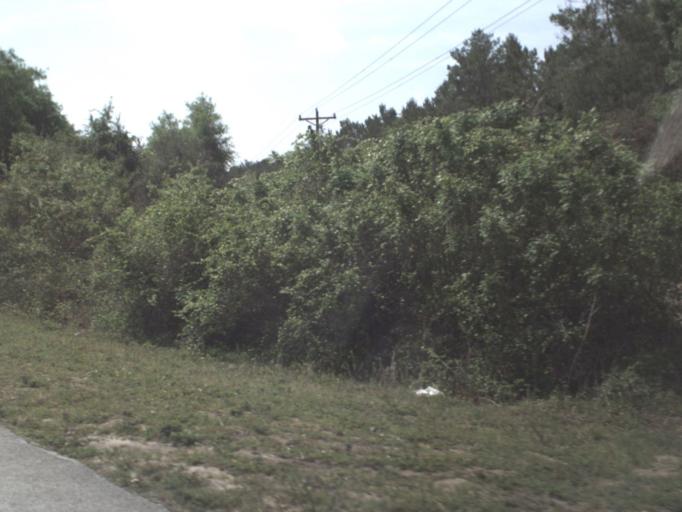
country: US
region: Florida
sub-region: Lake County
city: Astor
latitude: 29.2905
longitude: -81.6554
